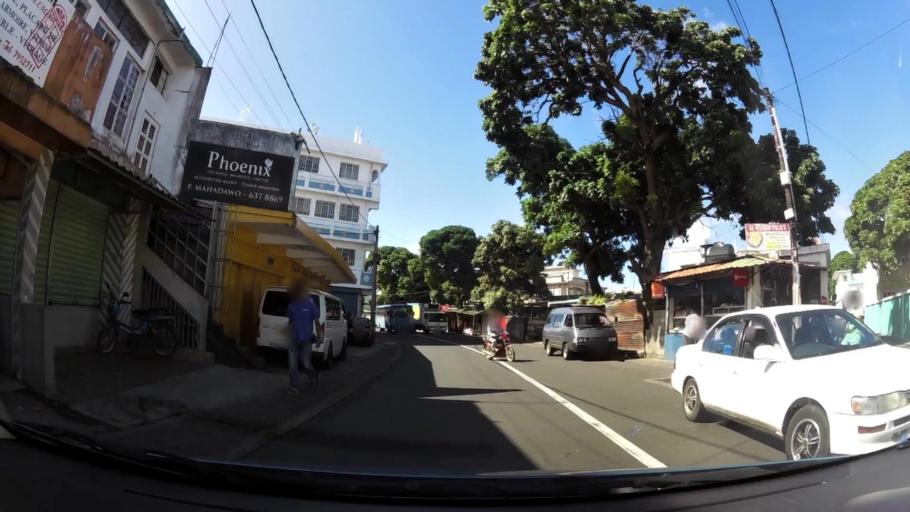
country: MU
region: Grand Port
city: Plaine Magnien
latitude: -20.4319
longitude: 57.6631
